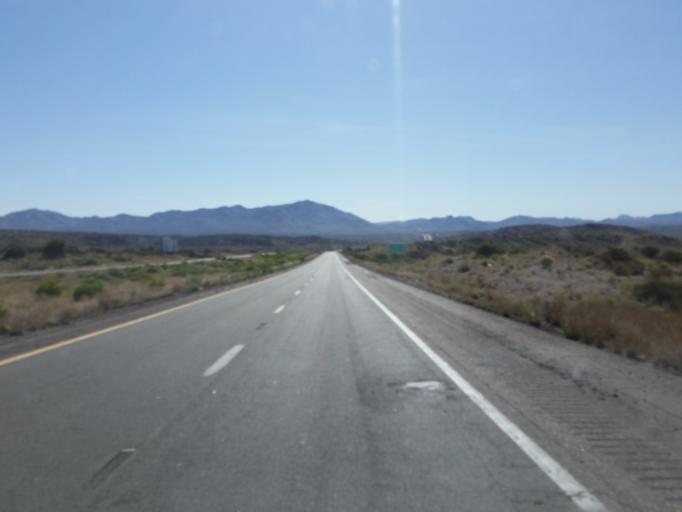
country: US
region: Arizona
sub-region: Mohave County
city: New Kingman-Butler
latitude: 35.1604
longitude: -113.6817
